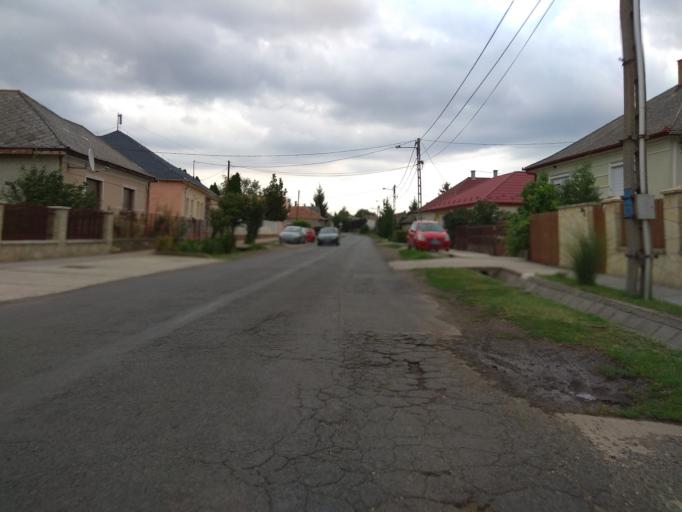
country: HU
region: Borsod-Abauj-Zemplen
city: Bekecs
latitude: 48.1580
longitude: 21.1542
